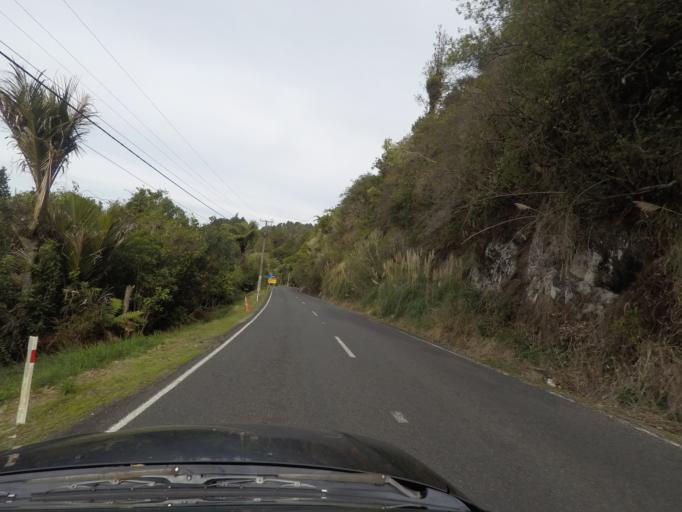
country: NZ
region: Auckland
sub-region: Auckland
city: Titirangi
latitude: -36.9367
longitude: 174.5794
